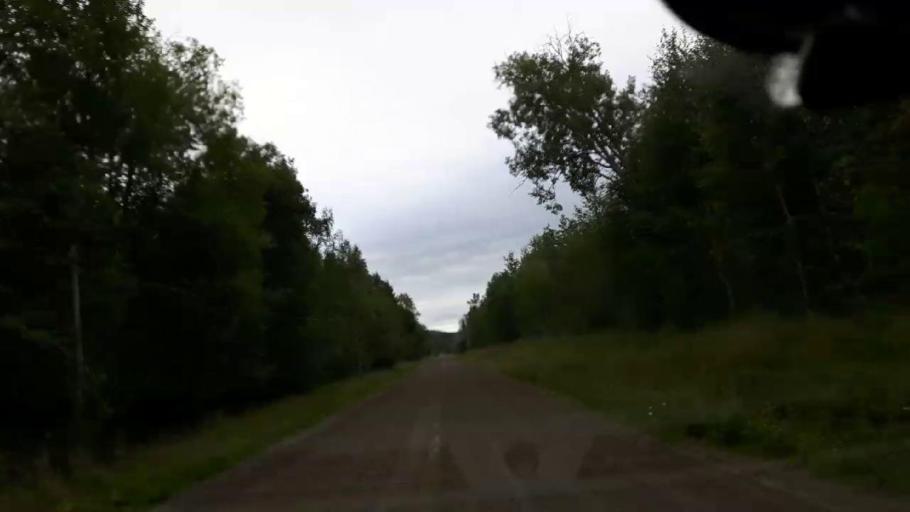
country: SE
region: Jaemtland
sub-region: Braecke Kommun
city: Braecke
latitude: 62.8999
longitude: 15.5998
